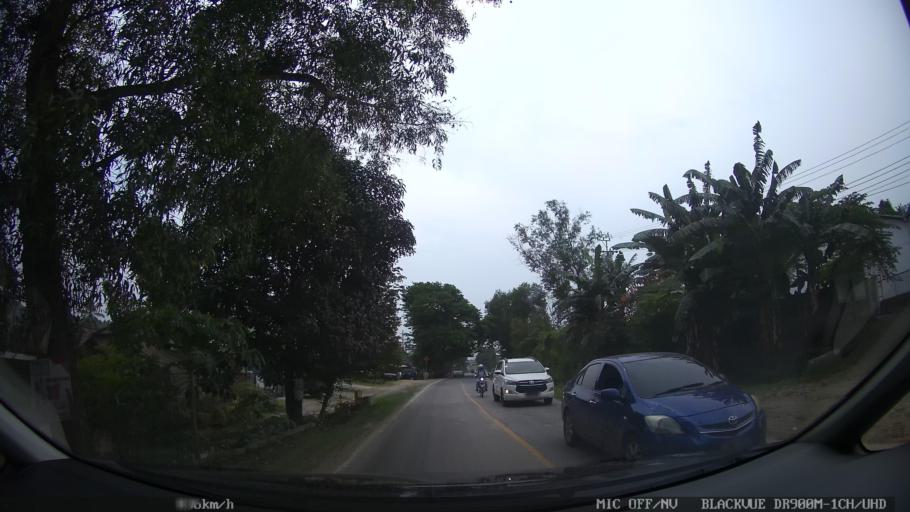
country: ID
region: Lampung
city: Panjang
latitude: -5.4027
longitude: 105.3518
